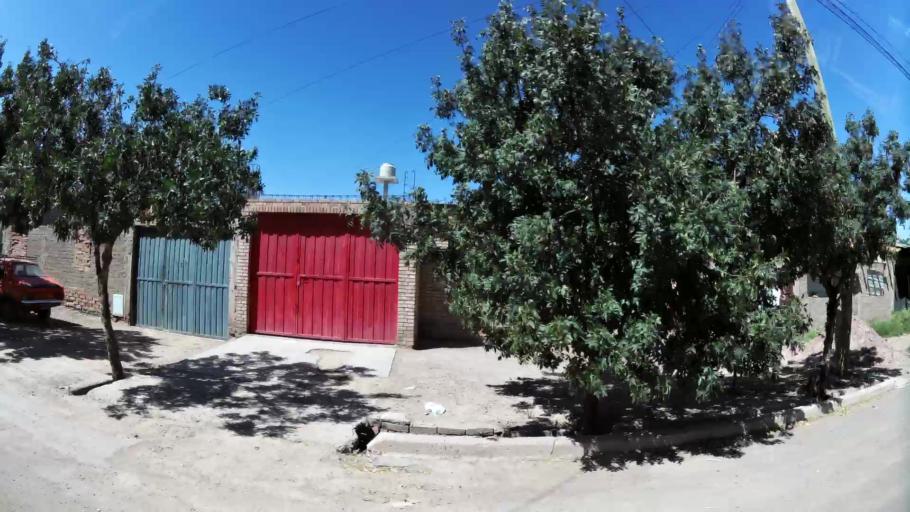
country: AR
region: Mendoza
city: Mendoza
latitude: -32.8771
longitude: -68.8101
